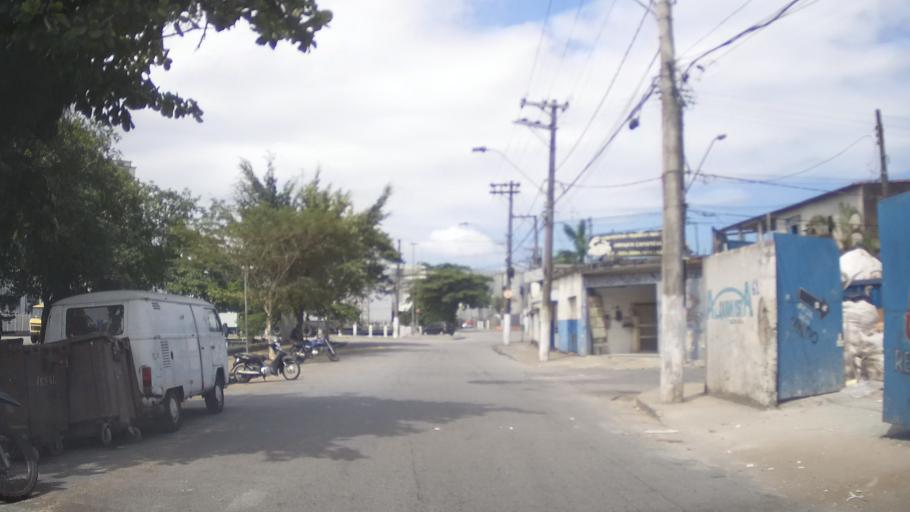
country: BR
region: Sao Paulo
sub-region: Santos
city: Santos
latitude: -23.9609
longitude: -46.3087
